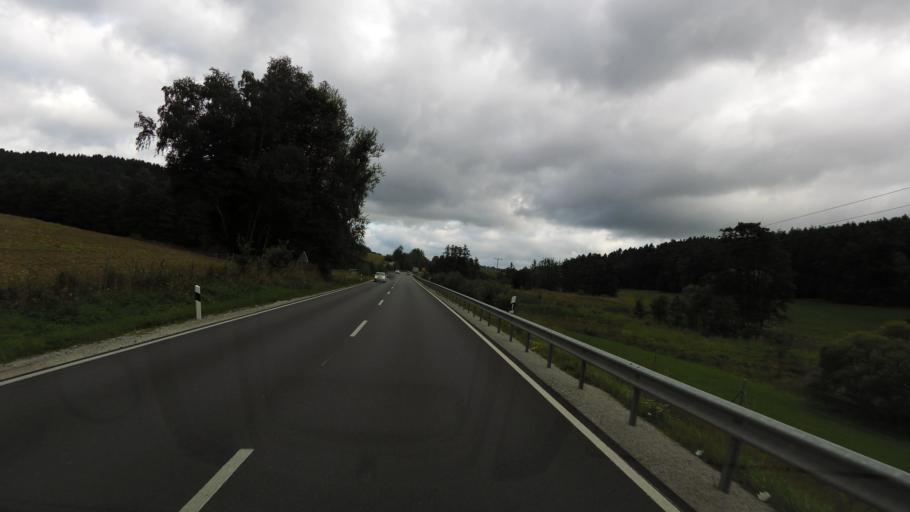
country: DE
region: Bavaria
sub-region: Upper Palatinate
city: Traitsching
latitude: 49.1425
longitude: 12.6502
